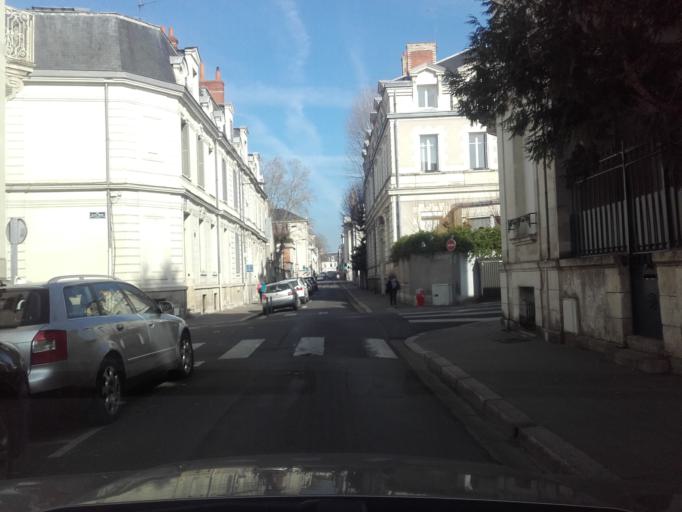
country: FR
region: Centre
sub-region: Departement d'Indre-et-Loire
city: Tours
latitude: 47.3882
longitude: 0.6847
